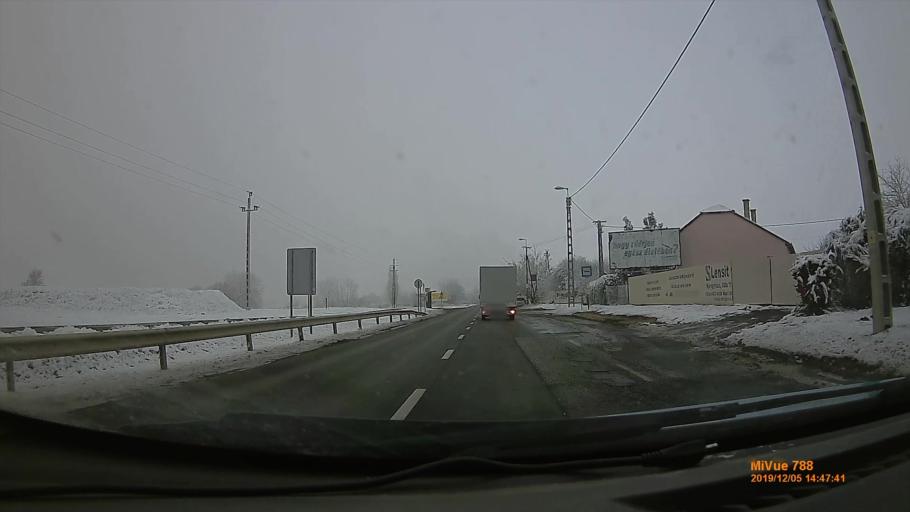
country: HU
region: Szabolcs-Szatmar-Bereg
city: Nyiregyhaza
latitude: 47.9711
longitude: 21.6934
